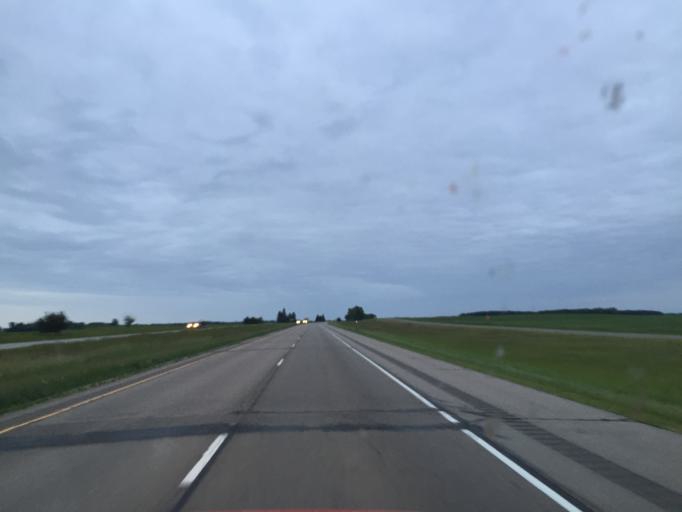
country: US
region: Minnesota
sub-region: Mower County
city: Austin
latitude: 43.6595
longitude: -93.0746
